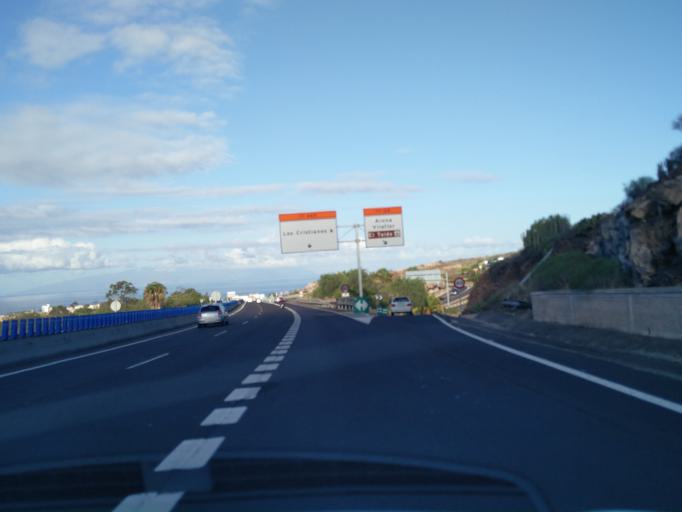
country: ES
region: Canary Islands
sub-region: Provincia de Santa Cruz de Tenerife
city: Playa de las Americas
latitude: 28.0641
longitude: -16.7094
